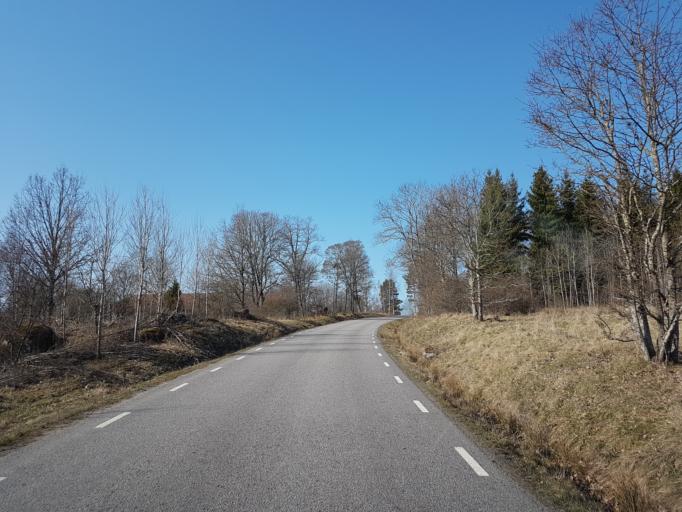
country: SE
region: OEstergoetland
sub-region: Valdemarsviks Kommun
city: Gusum
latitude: 58.1959
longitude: 16.3377
